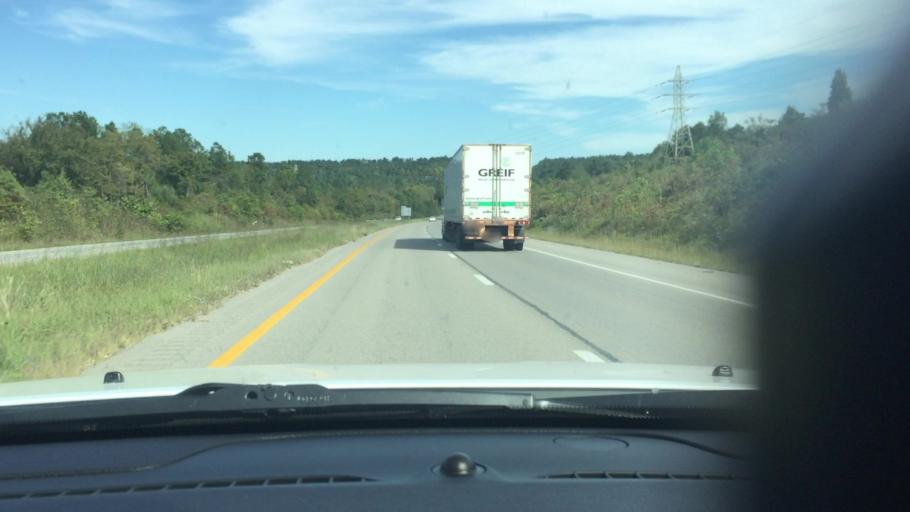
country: US
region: Kentucky
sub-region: Caldwell County
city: Princeton
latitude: 37.1388
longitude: -87.8520
